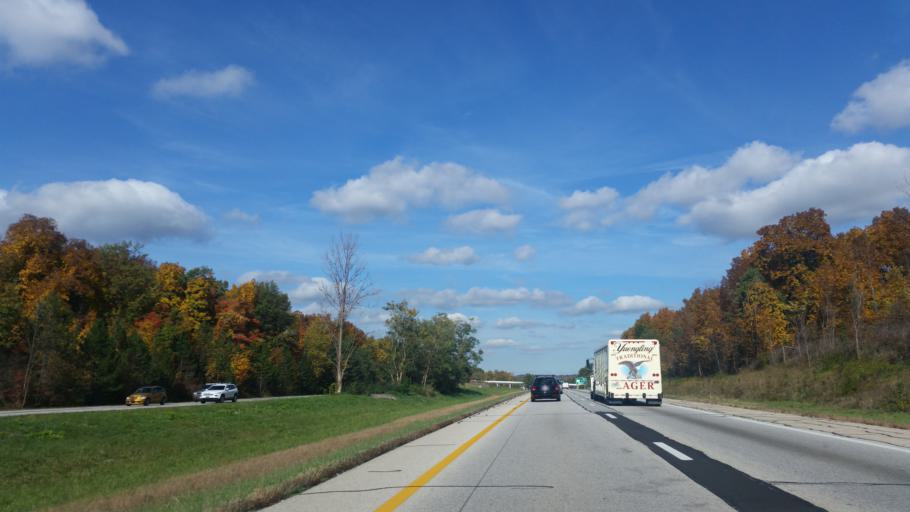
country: US
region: Ohio
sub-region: Summit County
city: Richfield
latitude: 41.2138
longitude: -81.6257
